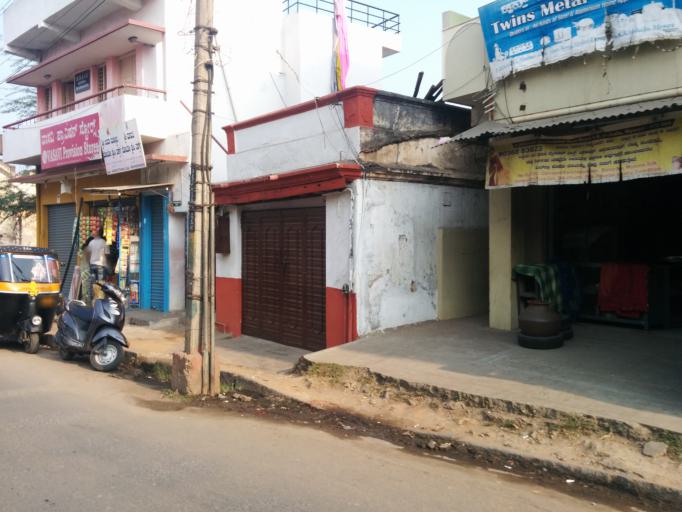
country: IN
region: Karnataka
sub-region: Mysore
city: Mysore
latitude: 12.2959
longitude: 76.6505
